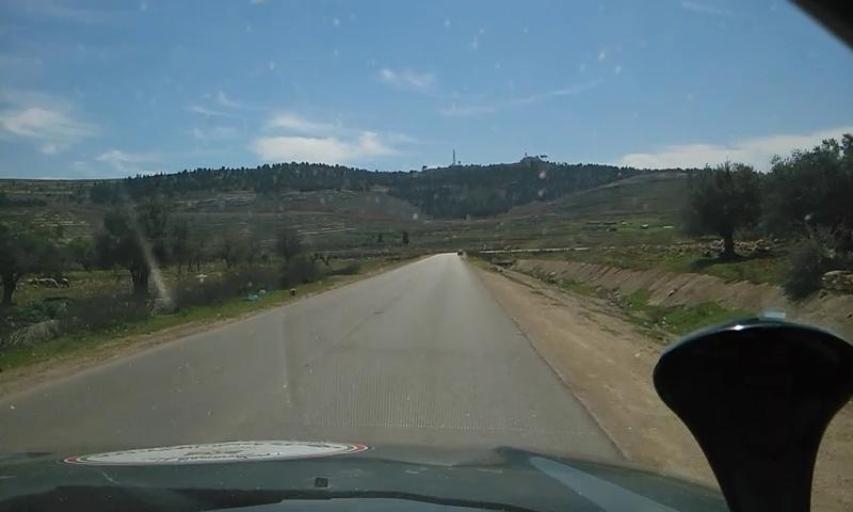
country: PS
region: West Bank
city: Al Jib
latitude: 31.8448
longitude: 35.1807
